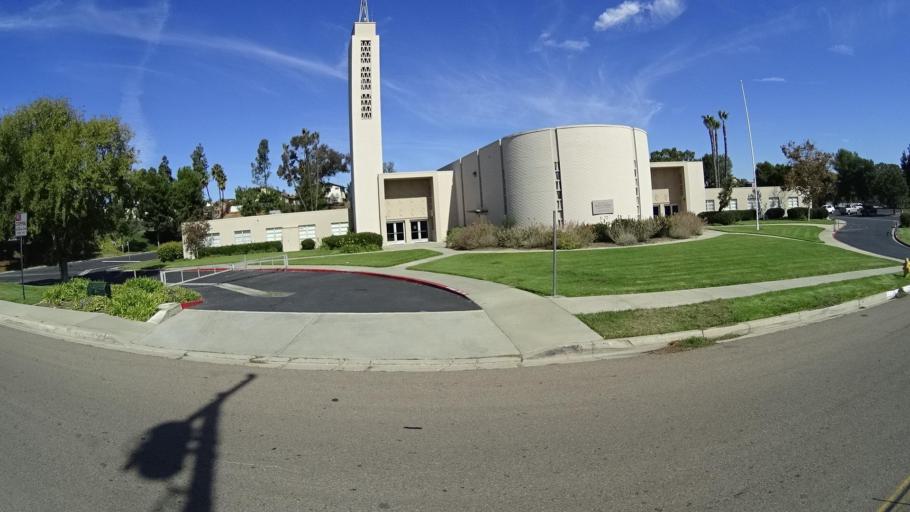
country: US
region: California
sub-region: San Diego County
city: Lemon Grove
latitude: 32.7249
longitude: -117.0176
